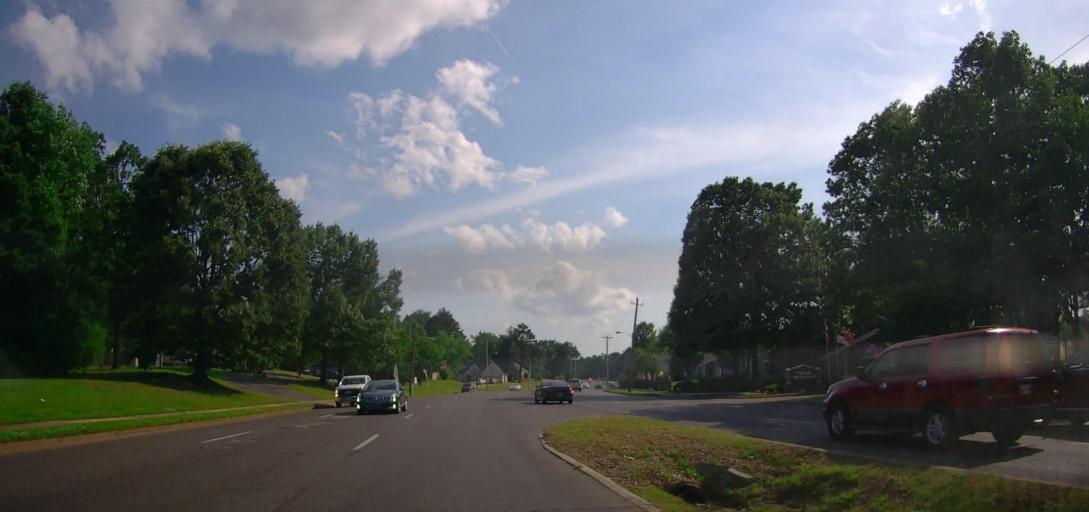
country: US
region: Tennessee
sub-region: Shelby County
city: Germantown
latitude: 35.0437
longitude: -89.8435
